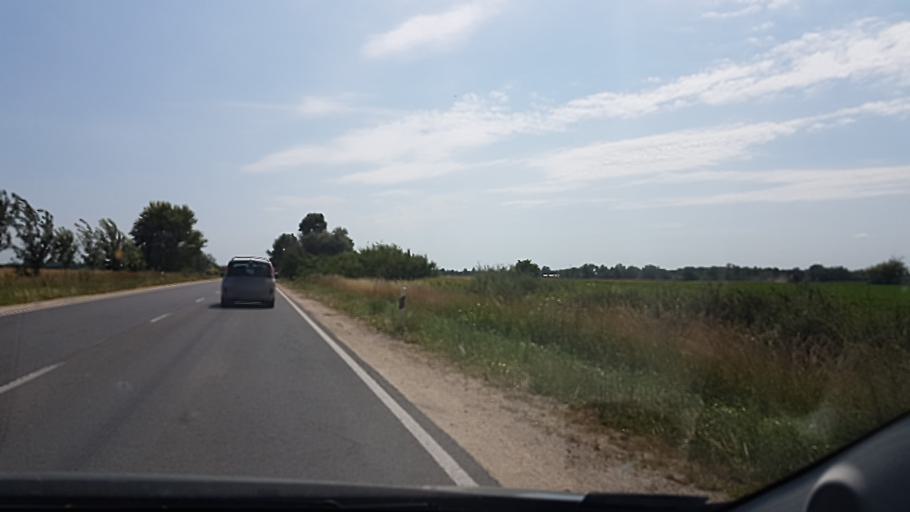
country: HU
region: Pest
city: Taksony
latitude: 47.3183
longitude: 19.0934
